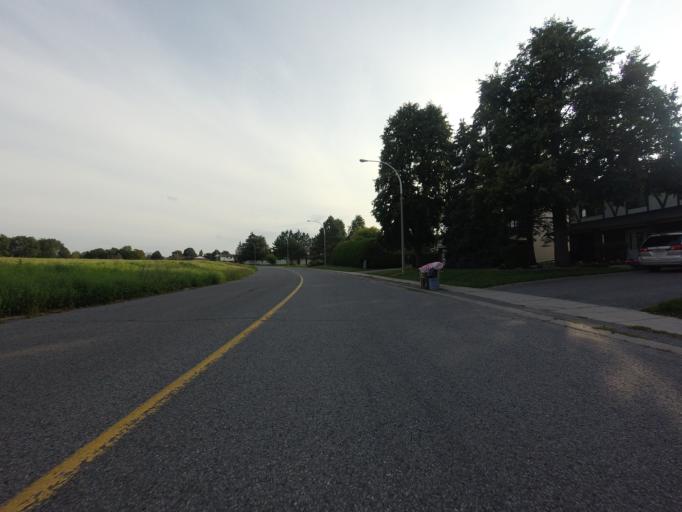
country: CA
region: Ontario
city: Bells Corners
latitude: 45.2890
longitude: -75.7492
